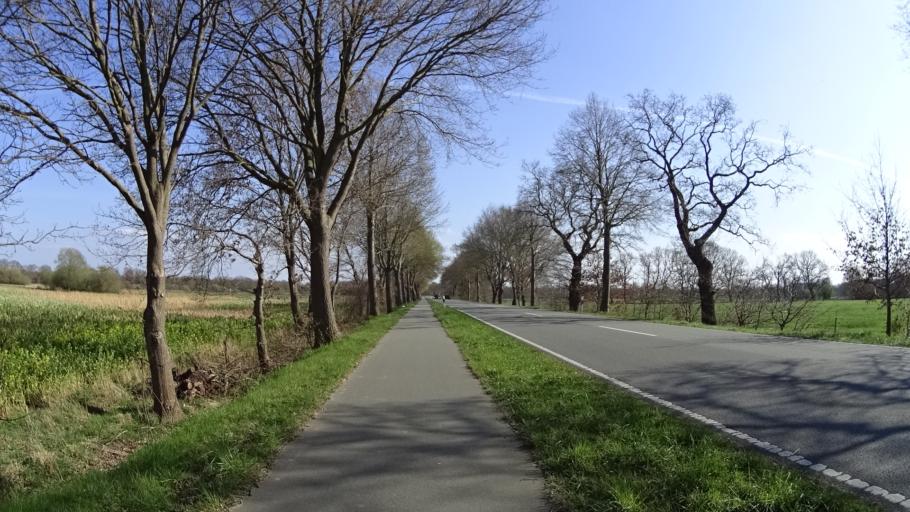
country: DE
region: Lower Saxony
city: Dorpen
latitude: 52.9757
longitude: 7.3101
